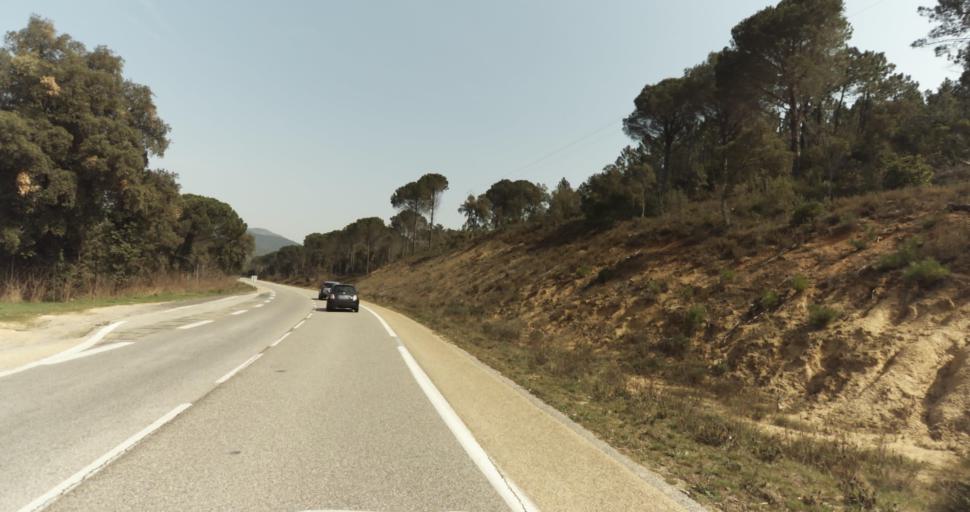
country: FR
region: Provence-Alpes-Cote d'Azur
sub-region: Departement du Var
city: Le Lavandou
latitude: 43.1908
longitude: 6.3740
